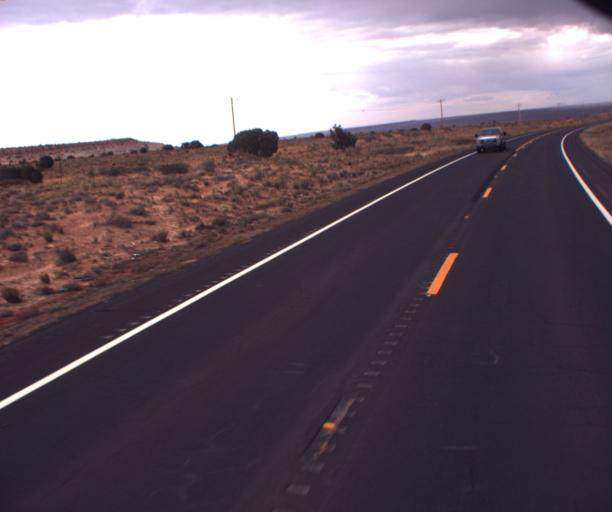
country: US
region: Arizona
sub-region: Coconino County
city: Tuba City
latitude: 36.2376
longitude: -111.0262
